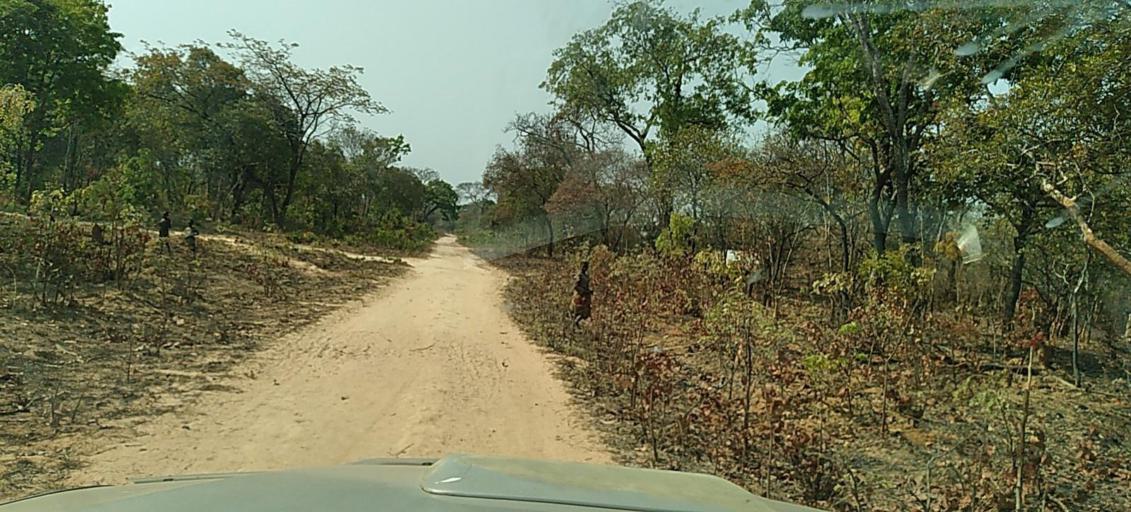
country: ZM
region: North-Western
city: Kasempa
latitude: -13.5447
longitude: 26.4088
